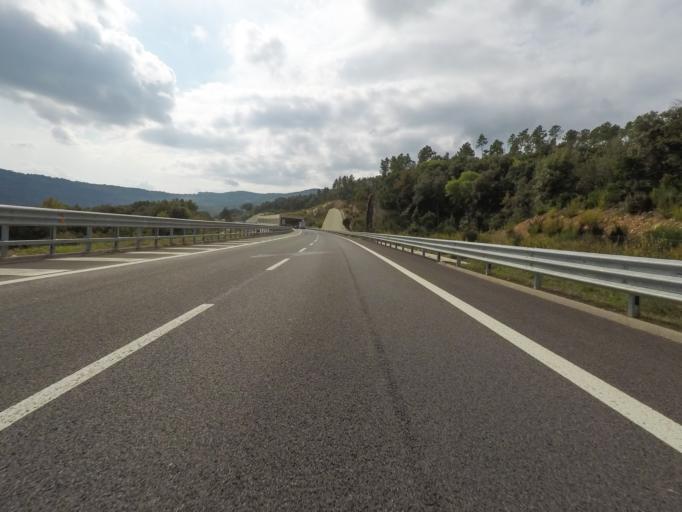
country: IT
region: Tuscany
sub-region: Provincia di Grosseto
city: Civitella Marittima
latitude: 43.0884
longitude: 11.2951
